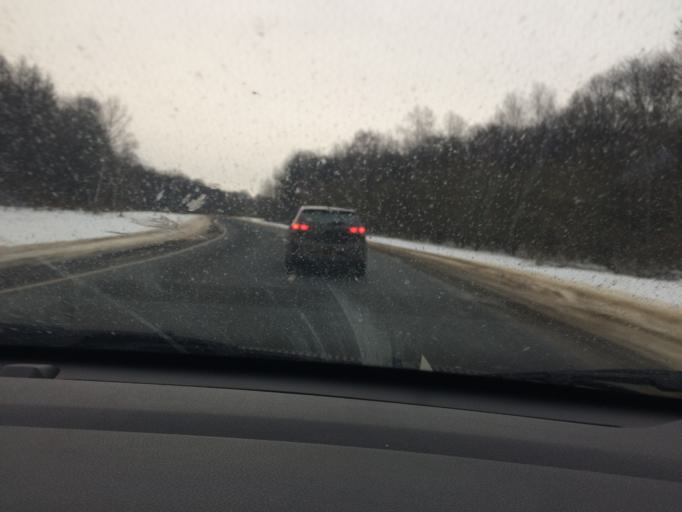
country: RU
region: Tula
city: Venev
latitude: 54.3359
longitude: 38.1332
